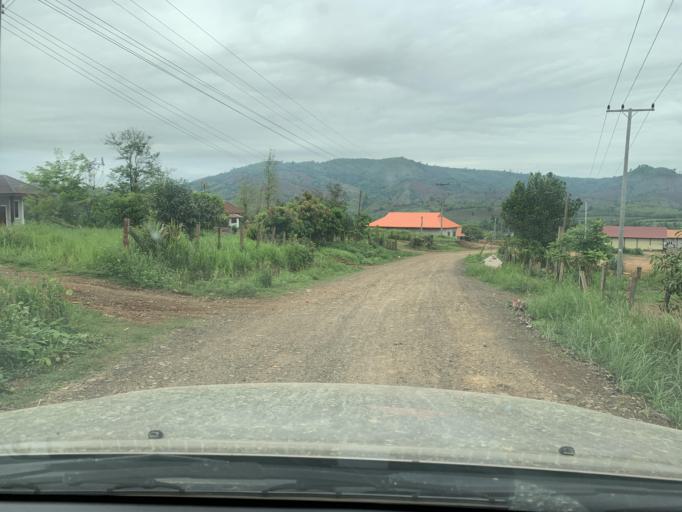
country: TH
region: Nan
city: Mae Charim
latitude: 18.4180
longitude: 101.4534
